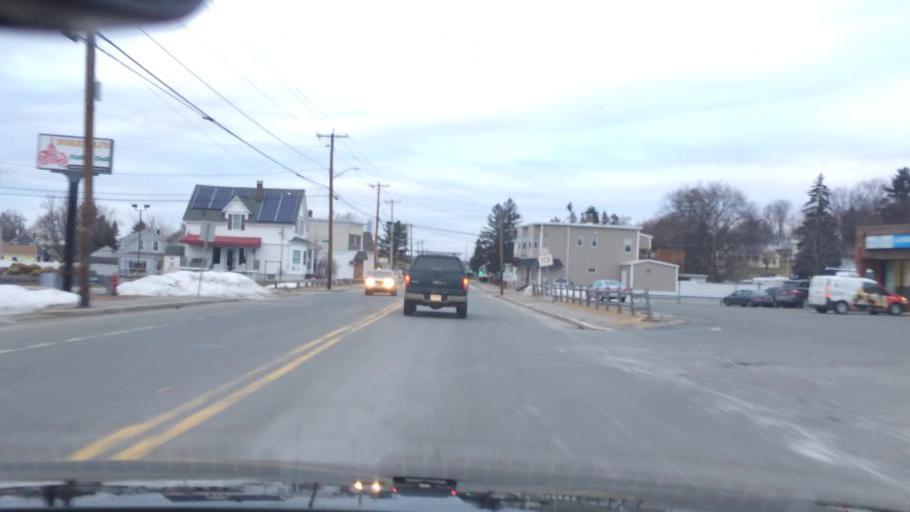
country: US
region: Massachusetts
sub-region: Essex County
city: North Andover
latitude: 42.7429
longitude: -71.1311
